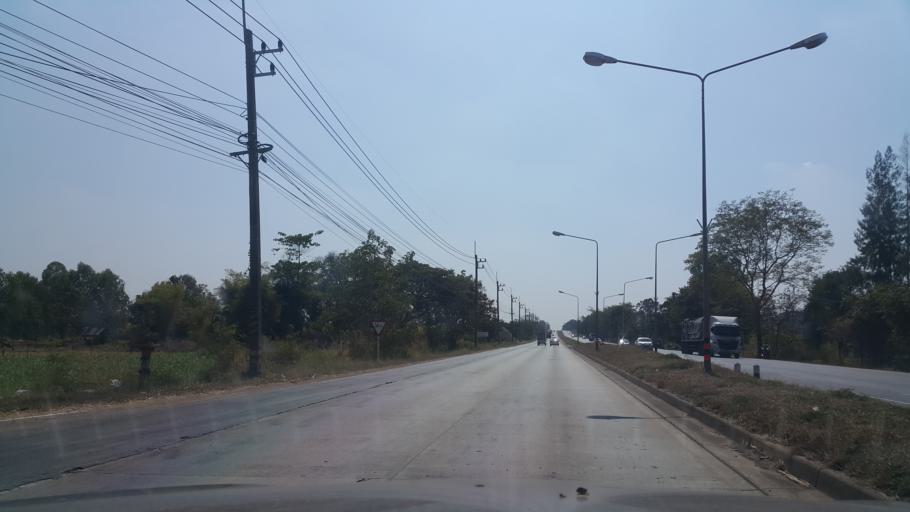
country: TH
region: Khon Kaen
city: Nam Phong
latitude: 16.8065
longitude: 102.8333
